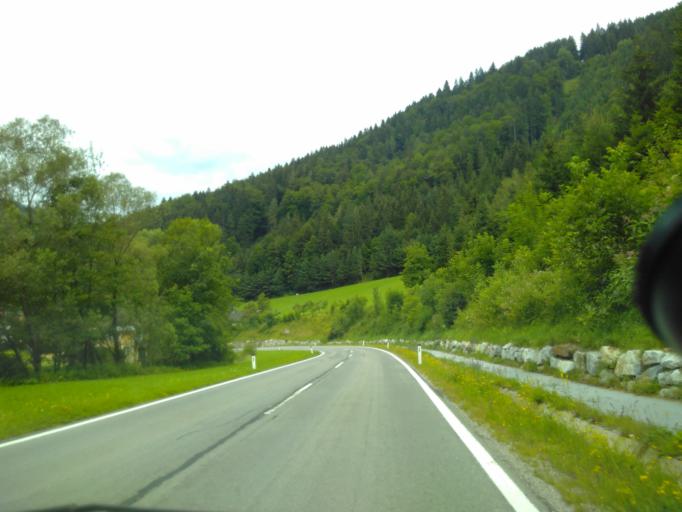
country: AT
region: Styria
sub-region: Politischer Bezirk Graz-Umgebung
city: Schrems bei Frohnleiten
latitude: 47.2790
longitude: 15.3752
